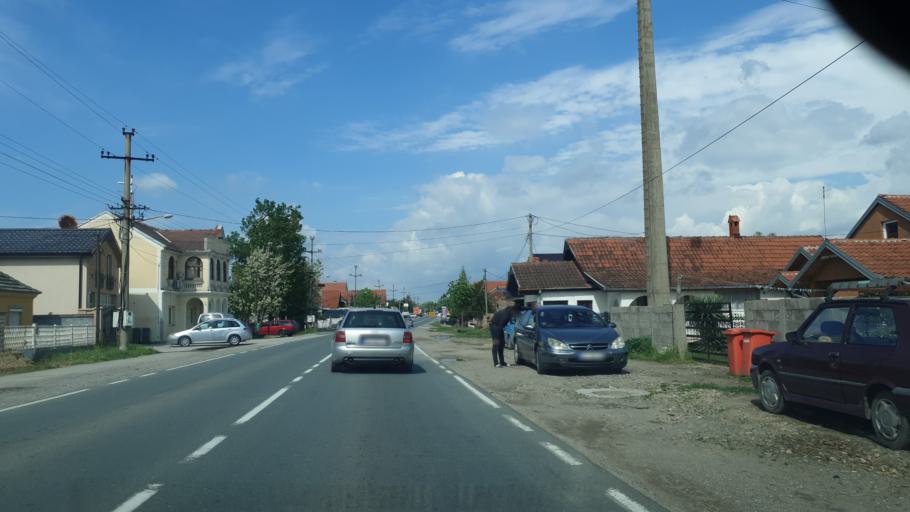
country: RS
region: Central Serbia
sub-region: Belgrade
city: Obrenovac
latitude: 44.6437
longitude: 20.1843
